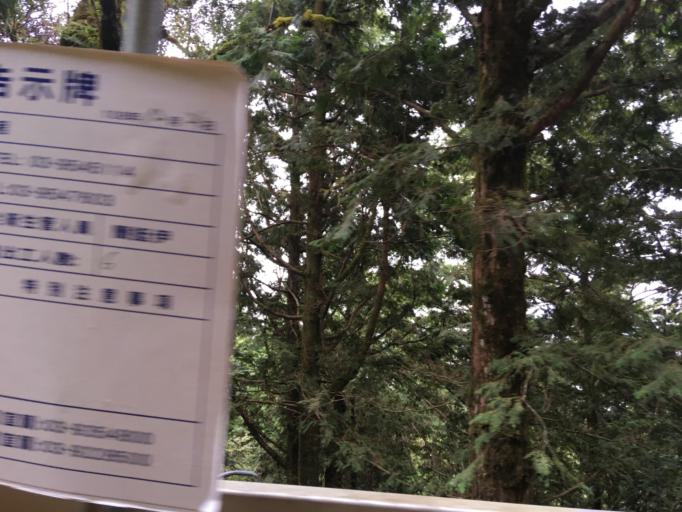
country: TW
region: Taiwan
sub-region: Yilan
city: Yilan
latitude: 24.4874
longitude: 121.5343
